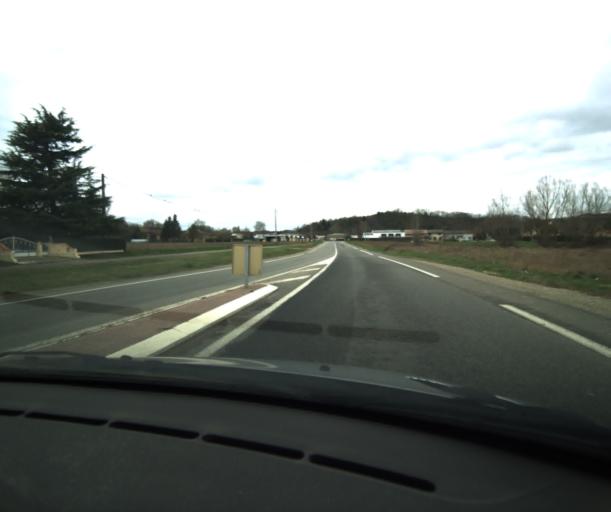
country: FR
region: Midi-Pyrenees
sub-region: Departement du Tarn-et-Garonne
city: Moissac
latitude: 44.1108
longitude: 1.1155
